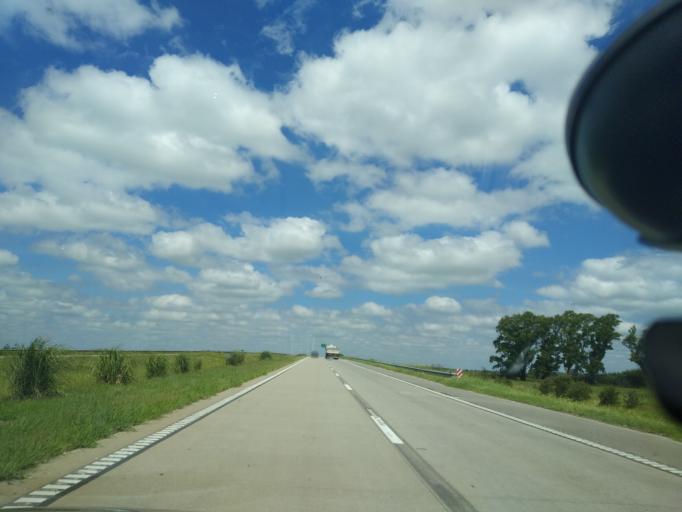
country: AR
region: Cordoba
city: Villa Maria
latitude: -32.4173
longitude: -63.1620
